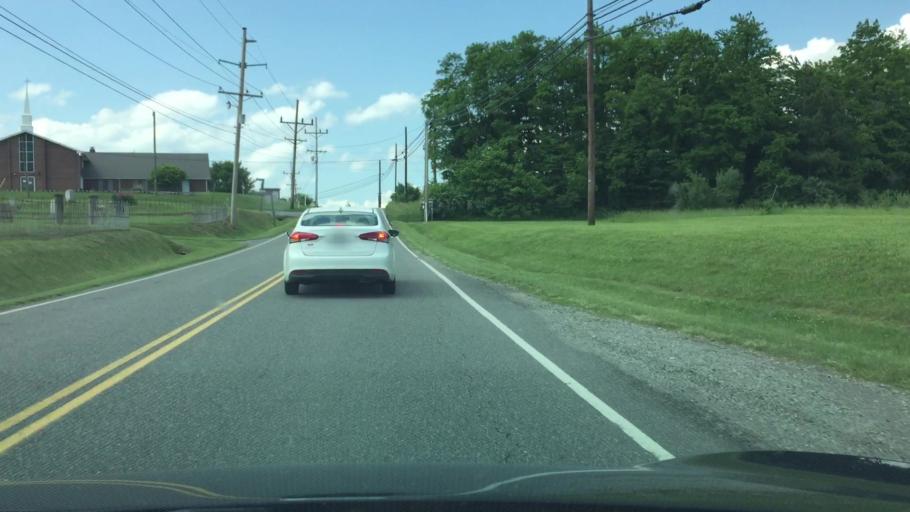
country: US
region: Virginia
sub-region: Pulaski County
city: Dublin
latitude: 37.0846
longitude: -80.6832
